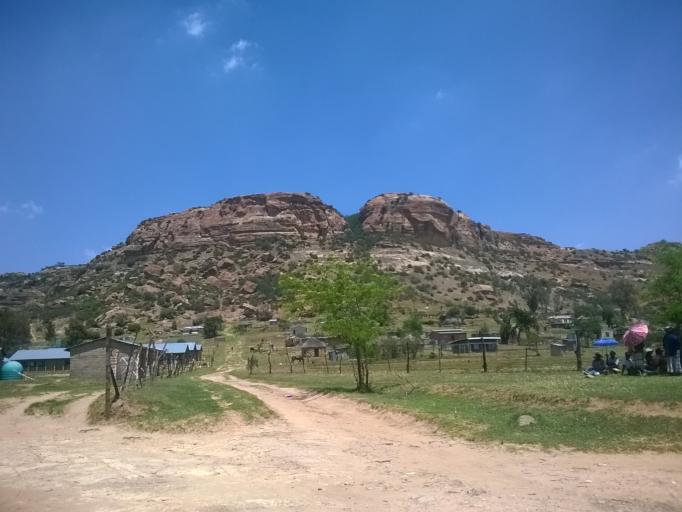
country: LS
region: Leribe
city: Leribe
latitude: -29.0025
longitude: 28.0409
